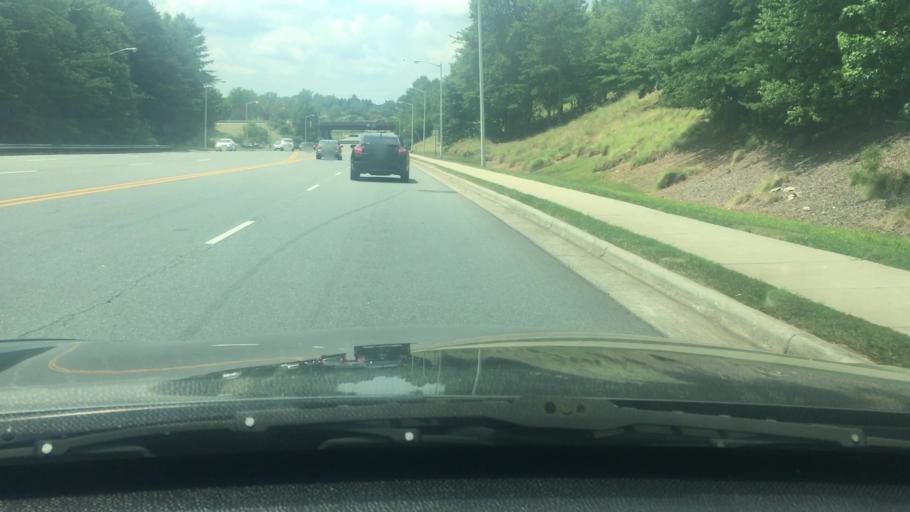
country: US
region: North Carolina
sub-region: Forsyth County
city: Winston-Salem
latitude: 36.0671
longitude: -80.2986
